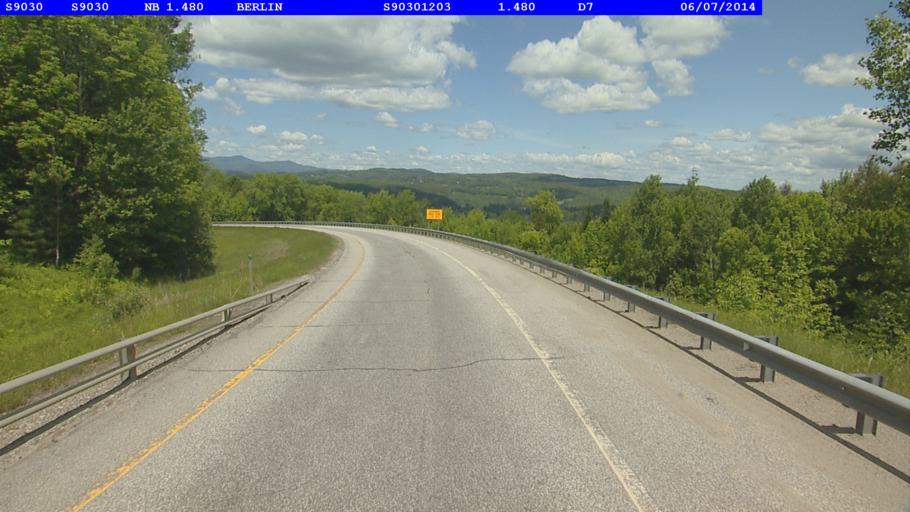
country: US
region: Vermont
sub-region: Washington County
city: Montpelier
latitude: 44.2218
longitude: -72.5558
